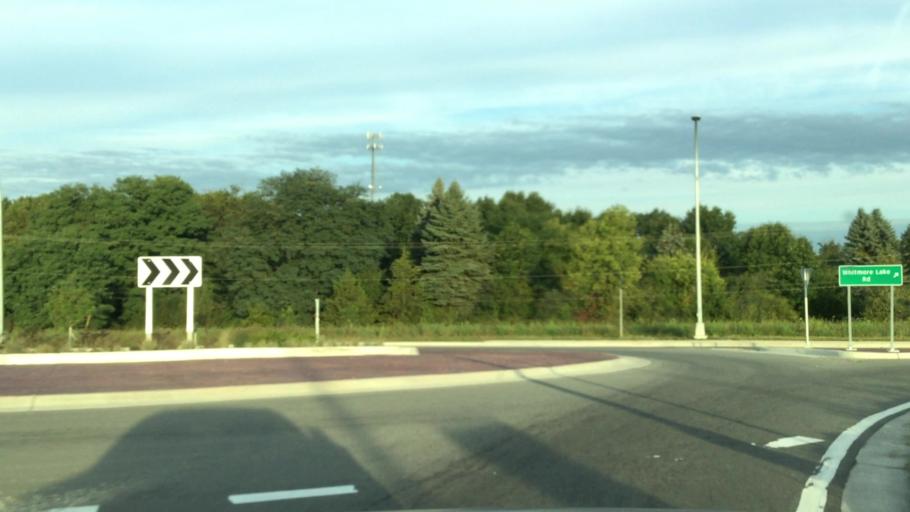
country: US
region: Michigan
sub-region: Livingston County
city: Whitmore Lake
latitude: 42.4294
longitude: -83.7688
